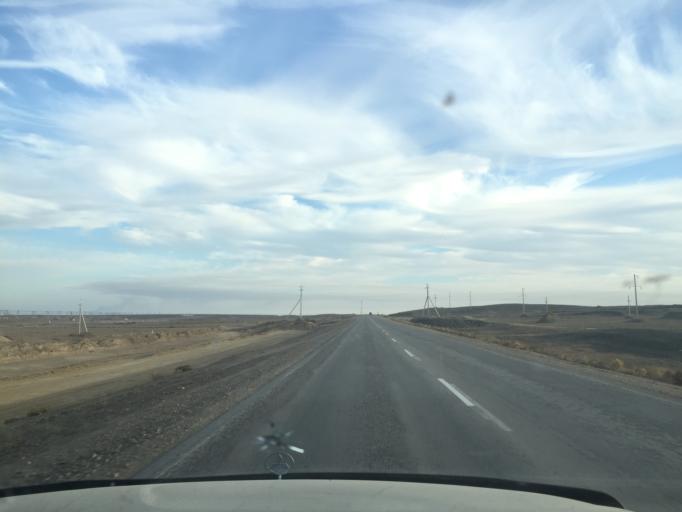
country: KZ
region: Almaty Oblysy
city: Ulken
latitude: 45.1773
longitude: 73.9285
